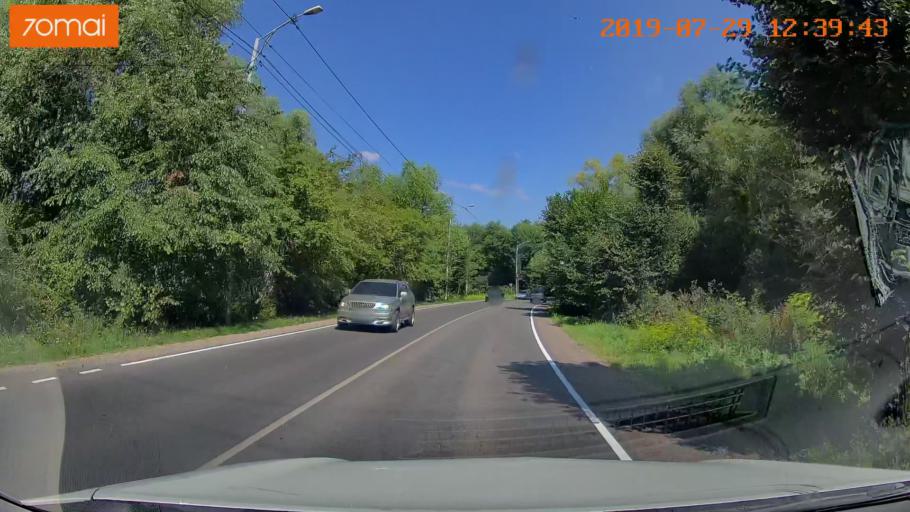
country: RU
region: Kaliningrad
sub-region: Gorod Kaliningrad
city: Kaliningrad
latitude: 54.6632
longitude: 20.5406
